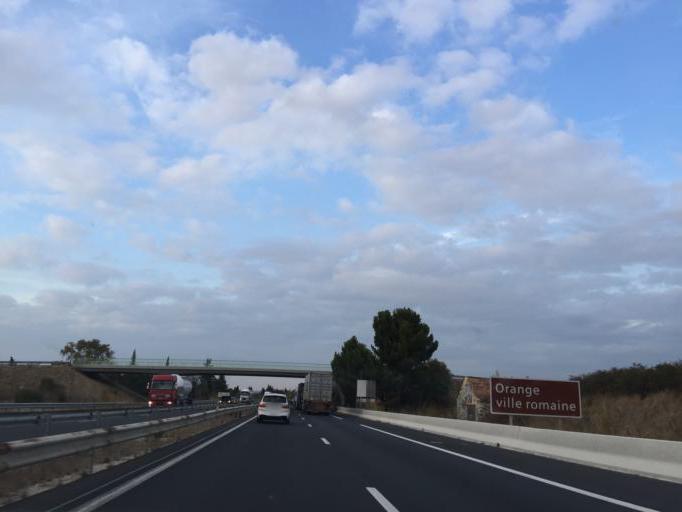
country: FR
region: Provence-Alpes-Cote d'Azur
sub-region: Departement du Vaucluse
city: Caderousse
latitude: 44.1102
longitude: 4.7887
